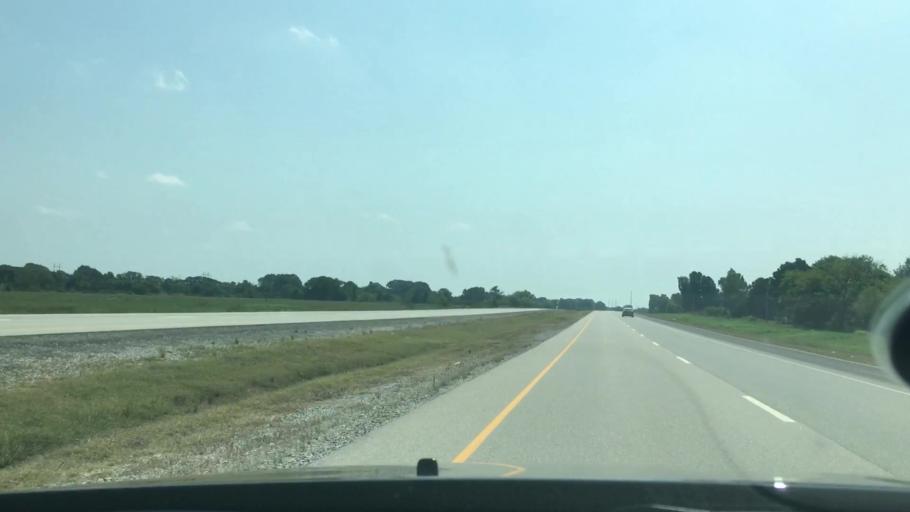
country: US
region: Oklahoma
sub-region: Atoka County
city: Atoka
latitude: 34.3398
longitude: -96.0652
